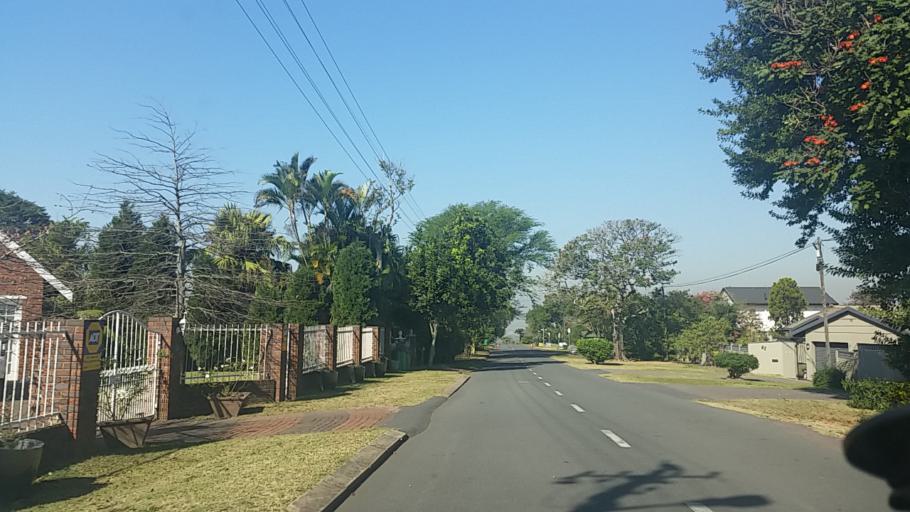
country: ZA
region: KwaZulu-Natal
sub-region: eThekwini Metropolitan Municipality
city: Berea
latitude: -29.8553
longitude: 30.9029
